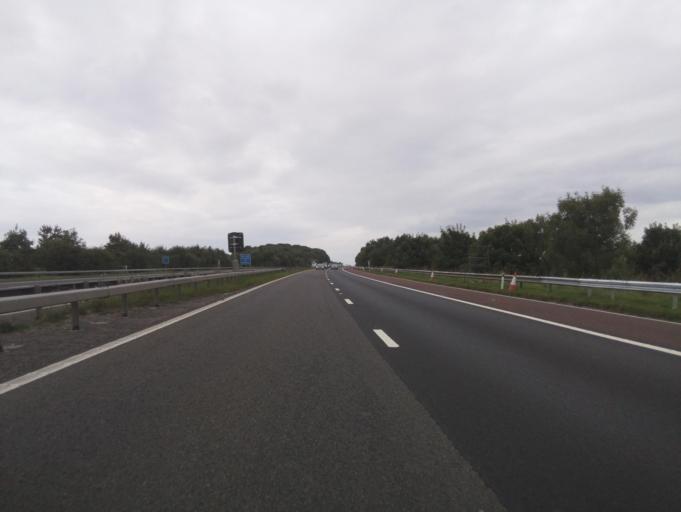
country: GB
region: England
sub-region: County Durham
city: Bishop Middleham
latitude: 54.6787
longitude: -1.5007
